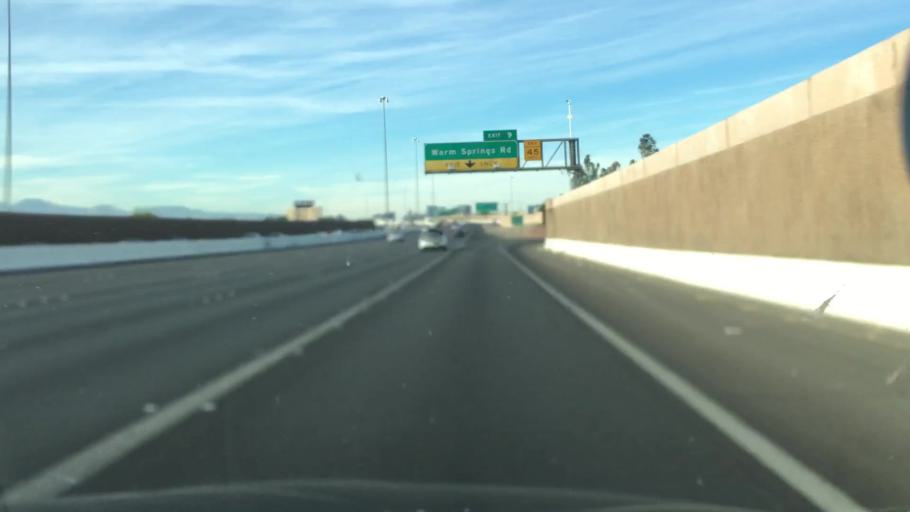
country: US
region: Nevada
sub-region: Clark County
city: Paradise
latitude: 36.0533
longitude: -115.1373
